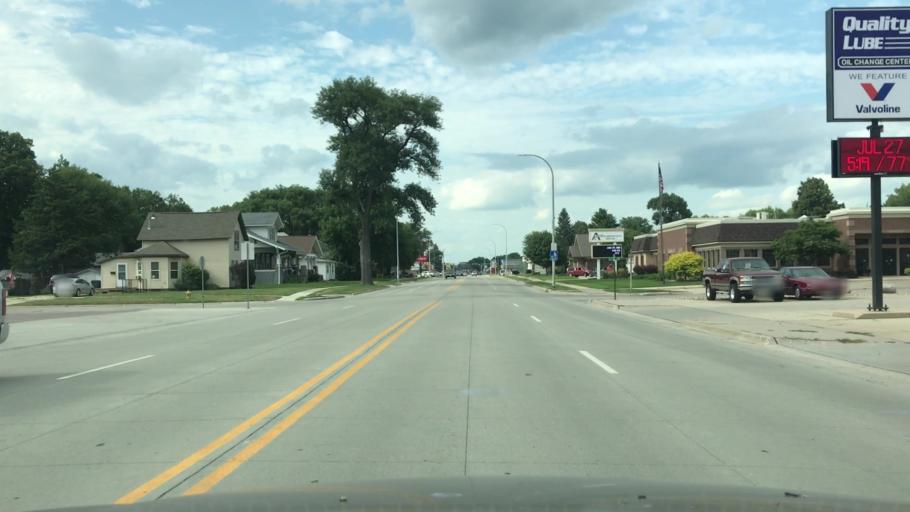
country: US
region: Iowa
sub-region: Plymouth County
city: Le Mars
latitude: 42.7889
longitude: -96.1738
